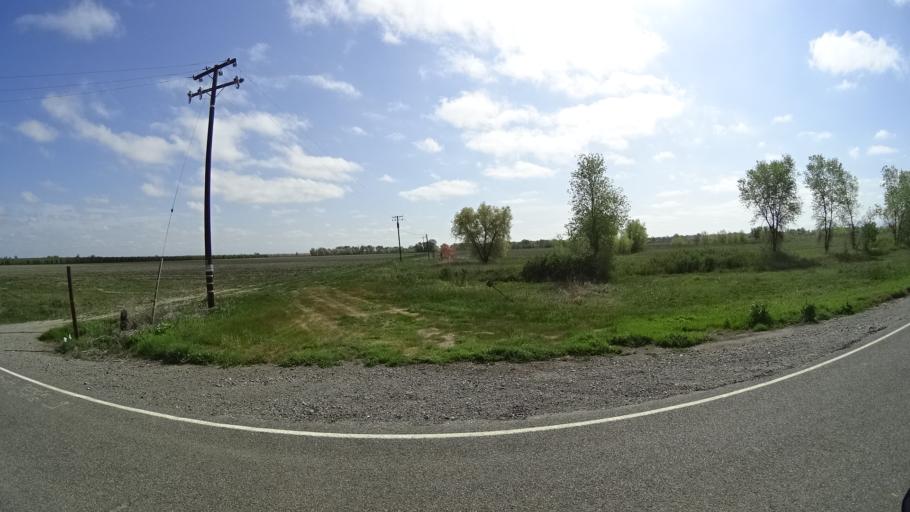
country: US
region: California
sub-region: Colusa County
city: Colusa
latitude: 39.4055
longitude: -121.9293
